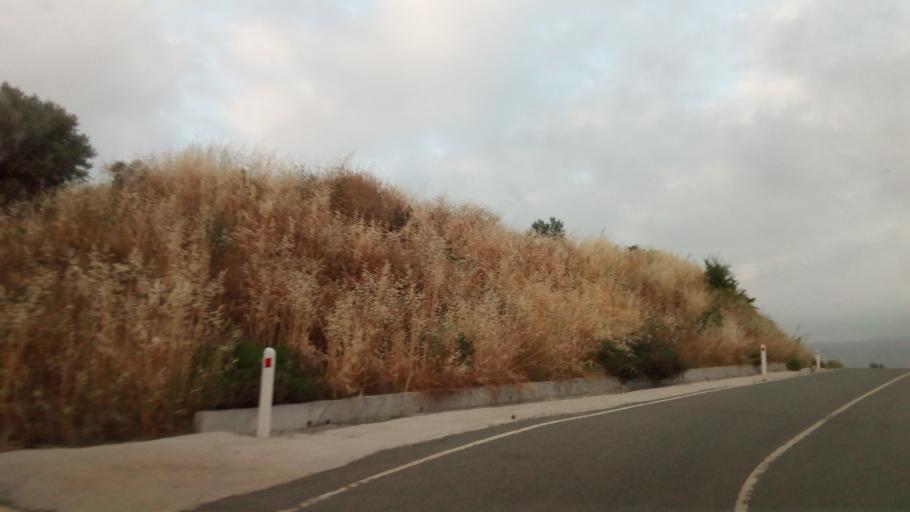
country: CY
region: Limassol
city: Pachna
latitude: 34.8620
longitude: 32.6429
